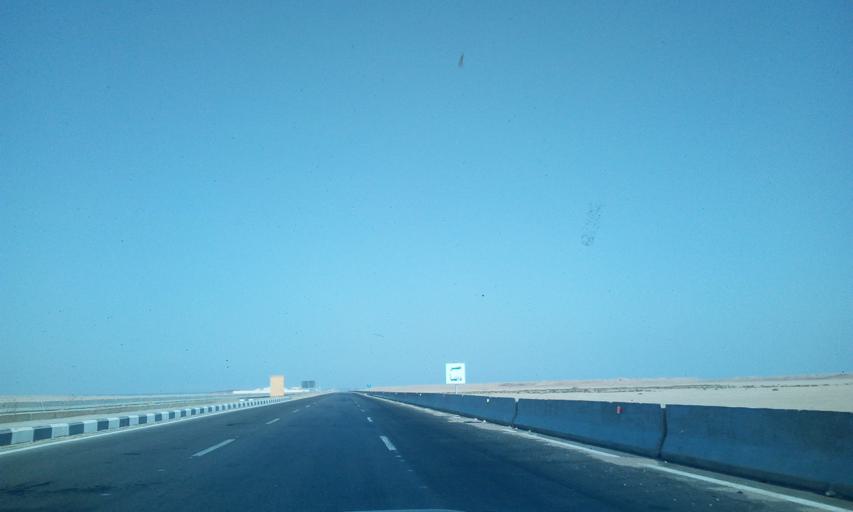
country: EG
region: As Suways
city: Ain Sukhna
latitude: 29.1105
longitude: 32.5536
